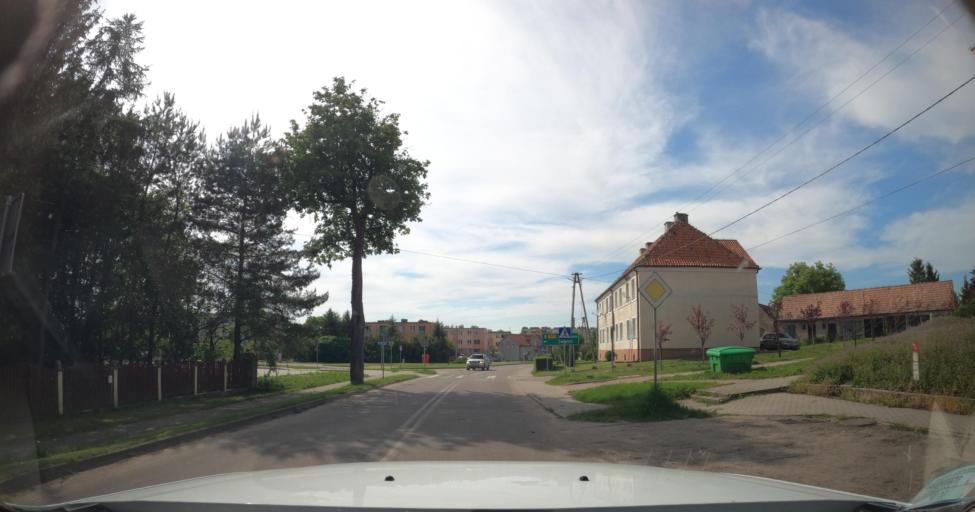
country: PL
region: Warmian-Masurian Voivodeship
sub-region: Powiat ostrodzki
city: Milakowo
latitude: 54.0081
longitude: 20.0793
